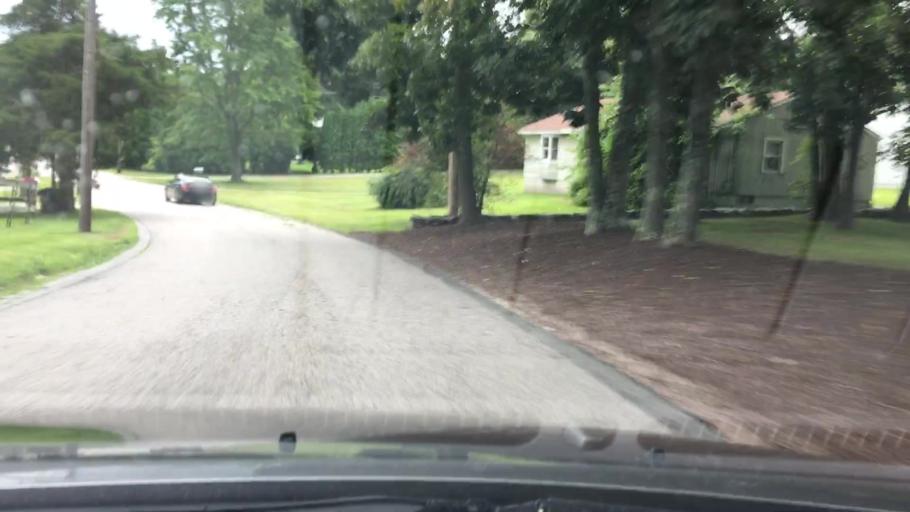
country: US
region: Rhode Island
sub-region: Providence County
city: Cumberland Hill
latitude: 42.0157
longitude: -71.4493
